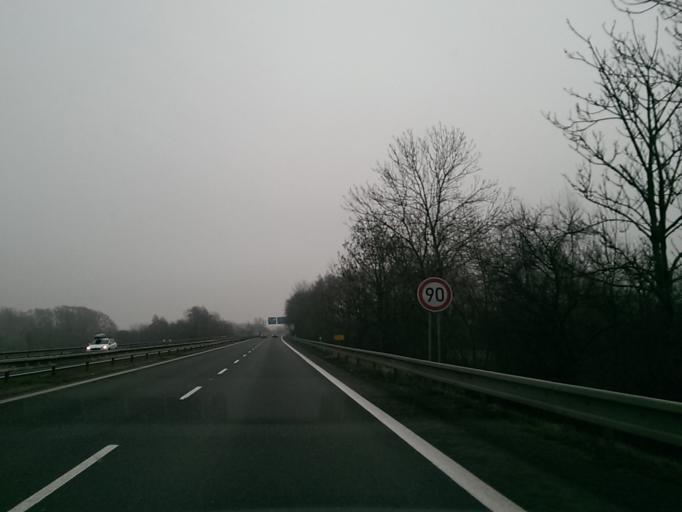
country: CZ
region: Olomoucky
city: Horka nad Moravou
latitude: 49.6077
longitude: 17.2071
